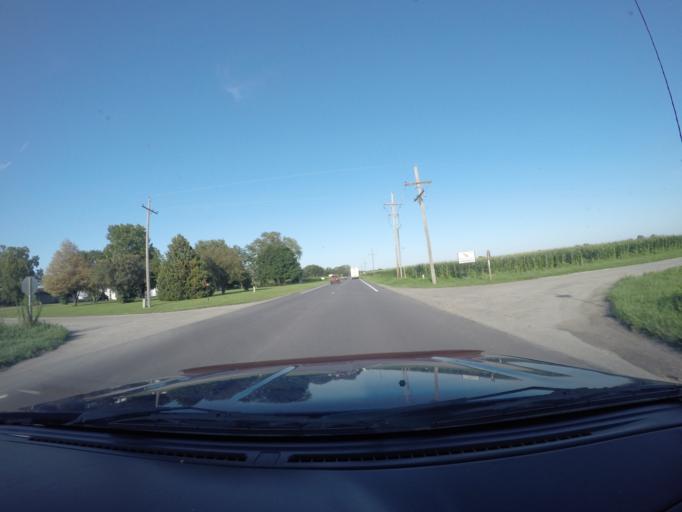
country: US
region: Kansas
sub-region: Douglas County
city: Lawrence
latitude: 39.0006
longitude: -95.2055
